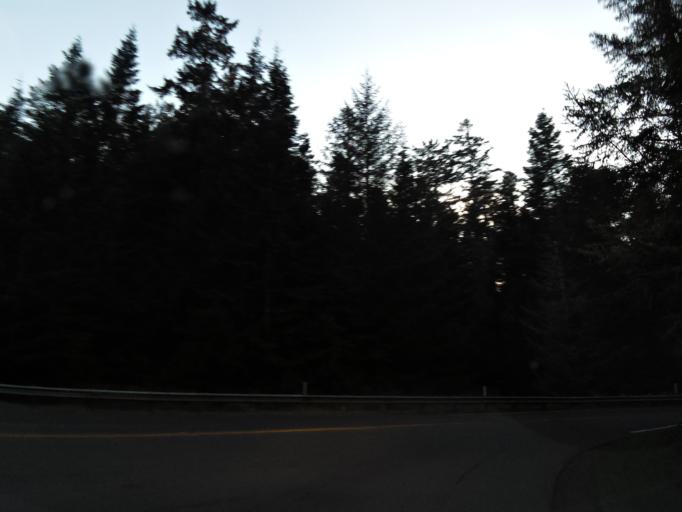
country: US
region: California
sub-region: Mendocino County
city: Fort Bragg
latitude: 39.3576
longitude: -123.8086
